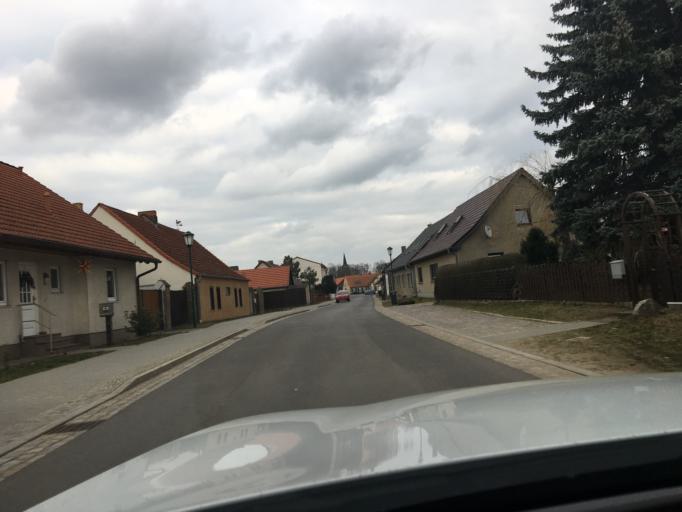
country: DE
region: Brandenburg
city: Liebenwalde
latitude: 52.8782
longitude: 13.4378
